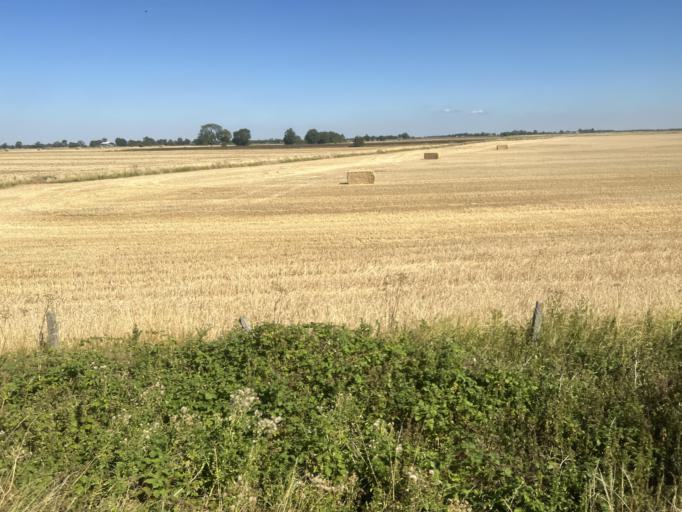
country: GB
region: England
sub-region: Lincolnshire
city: Donington
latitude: 52.9665
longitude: -0.2304
